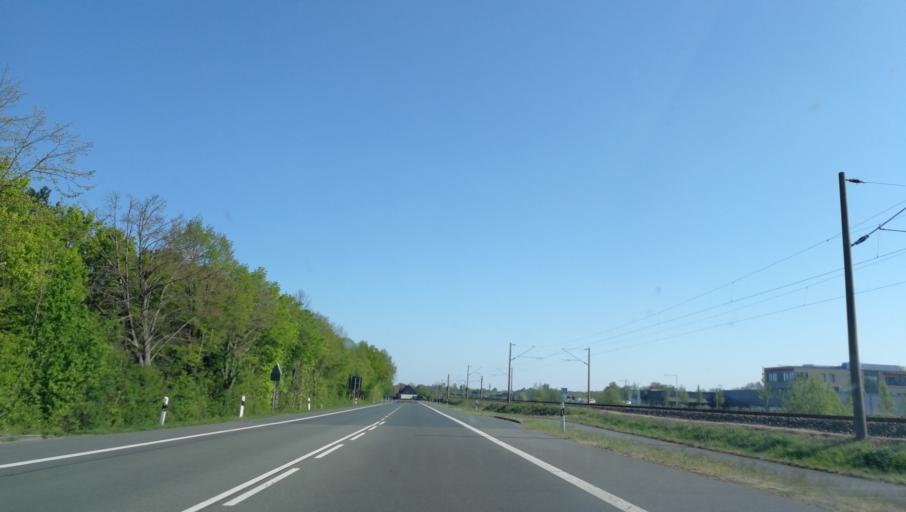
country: DE
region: North Rhine-Westphalia
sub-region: Regierungsbezirk Munster
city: Rheine
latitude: 52.2596
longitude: 7.4537
